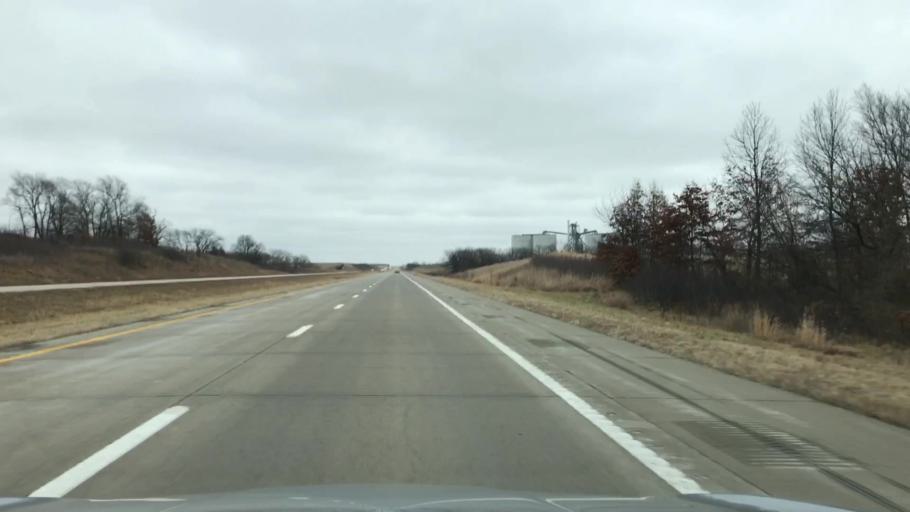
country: US
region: Missouri
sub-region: Caldwell County
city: Hamilton
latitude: 39.7353
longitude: -93.9168
